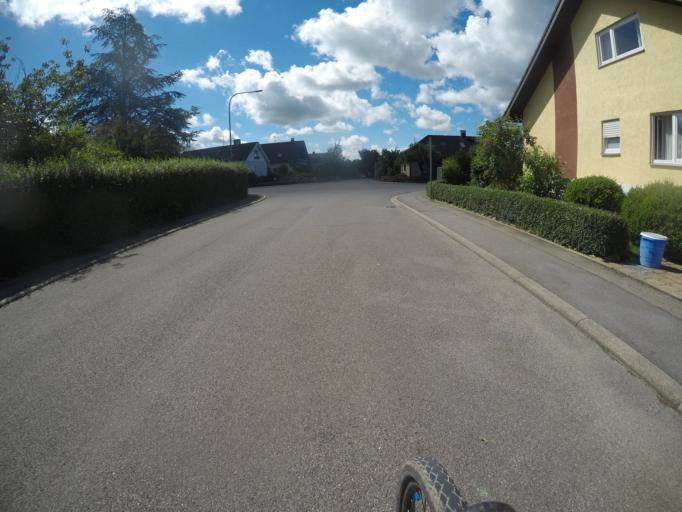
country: DE
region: Baden-Wuerttemberg
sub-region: Regierungsbezirk Stuttgart
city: Unterjettingen
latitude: 48.5613
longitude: 8.7861
